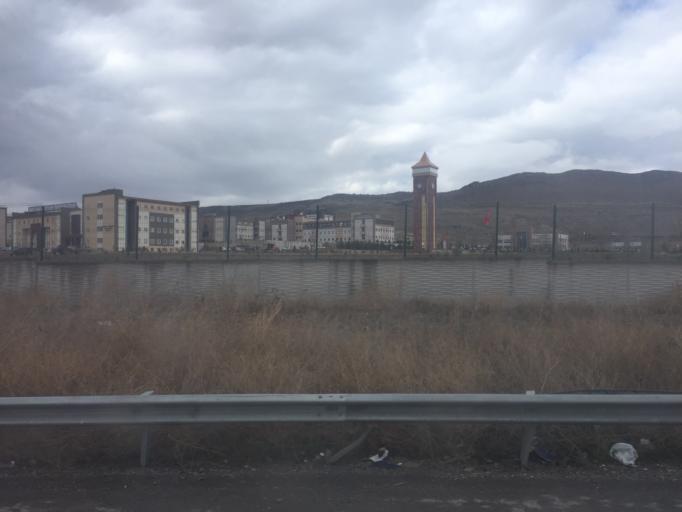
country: TR
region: Kayseri
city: Erkilet
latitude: 38.7838
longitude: 35.4104
